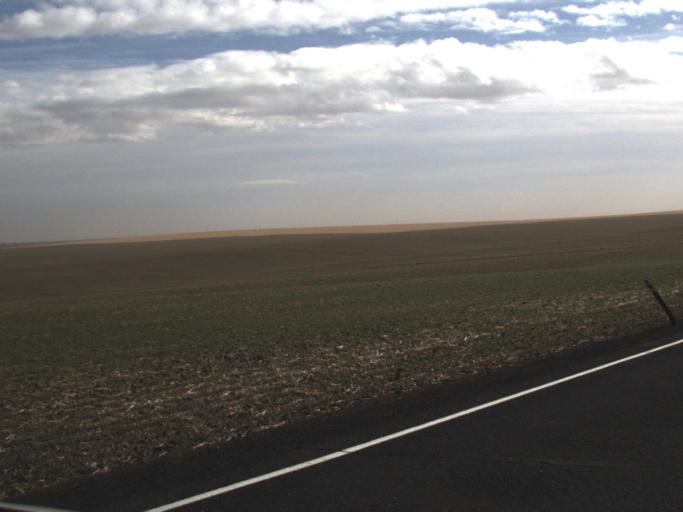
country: US
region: Washington
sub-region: Okanogan County
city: Coulee Dam
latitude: 47.6548
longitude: -118.7212
